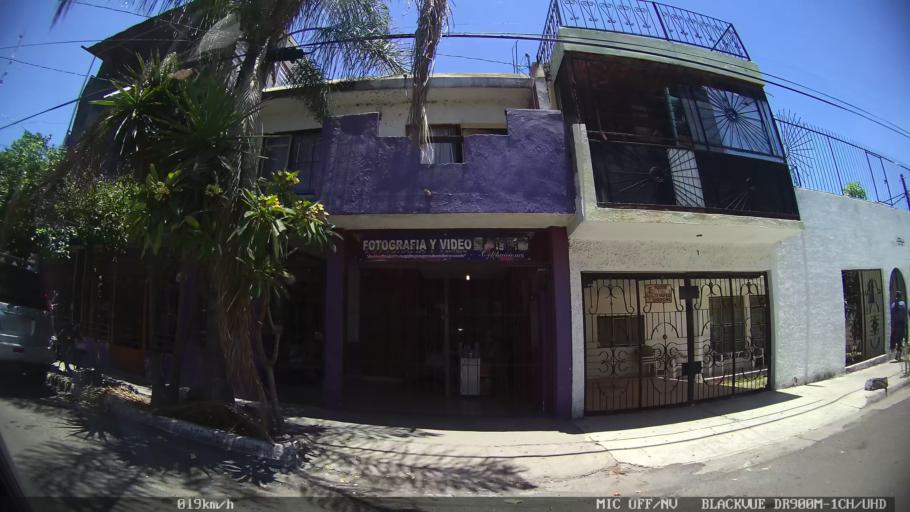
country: MX
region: Jalisco
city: Tlaquepaque
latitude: 20.6678
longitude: -103.2954
